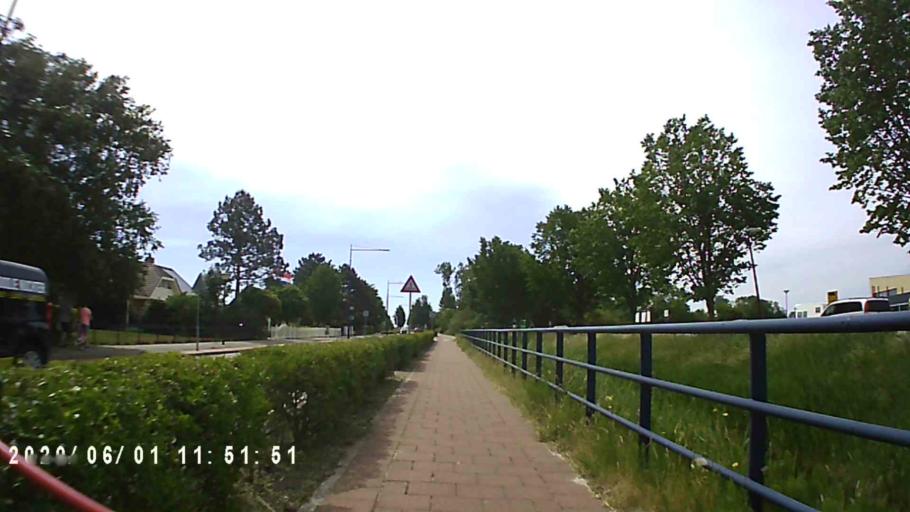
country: NL
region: Friesland
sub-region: Gemeente Harlingen
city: Harlingen
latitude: 53.1651
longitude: 5.4273
